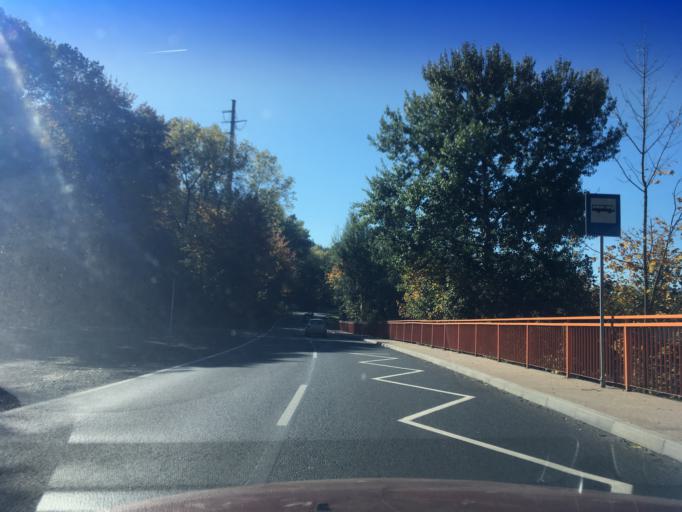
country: DE
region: Saxony
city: Hirschfelde
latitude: 50.9375
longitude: 14.8947
